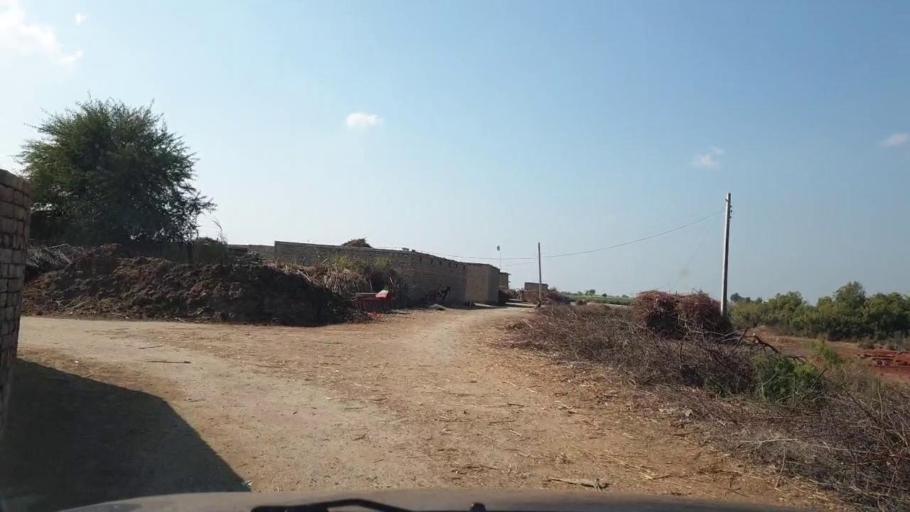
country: PK
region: Sindh
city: Khadro
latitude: 26.0785
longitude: 68.7440
